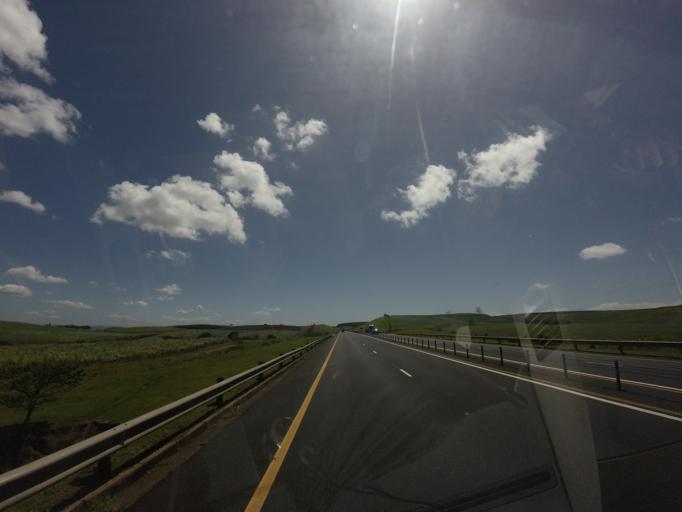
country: ZA
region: KwaZulu-Natal
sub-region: uThungulu District Municipality
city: Eshowe
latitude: -29.0513
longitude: 31.6365
